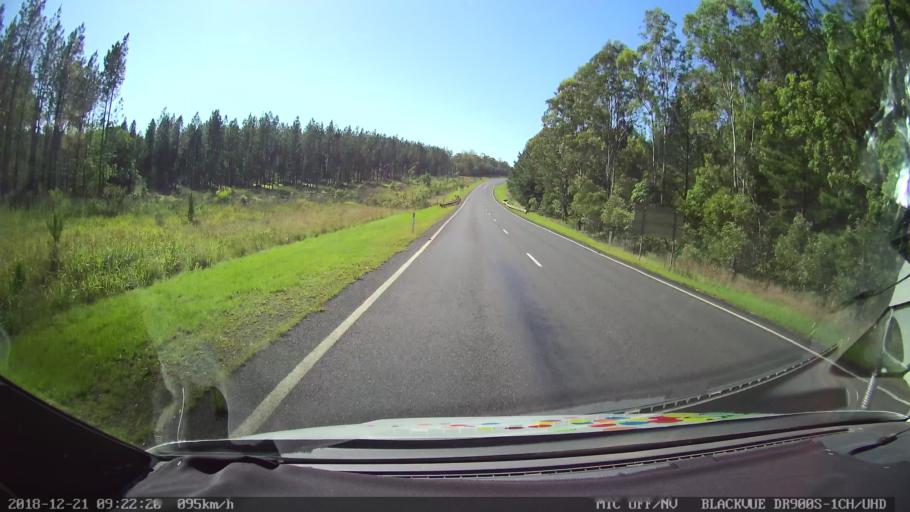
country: AU
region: New South Wales
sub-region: Clarence Valley
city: Maclean
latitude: -29.3406
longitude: 153.0044
